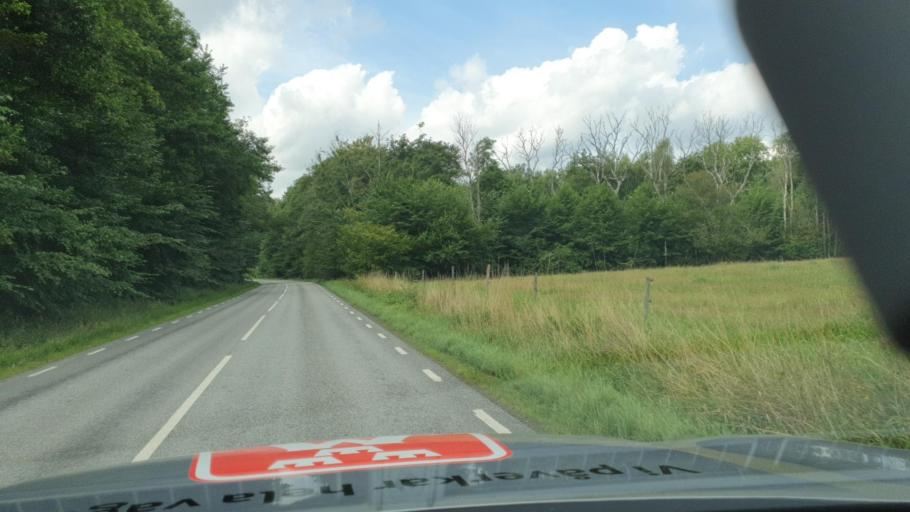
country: SE
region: Skane
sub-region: Ostra Goinge Kommun
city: Knislinge
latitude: 56.1898
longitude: 14.0270
